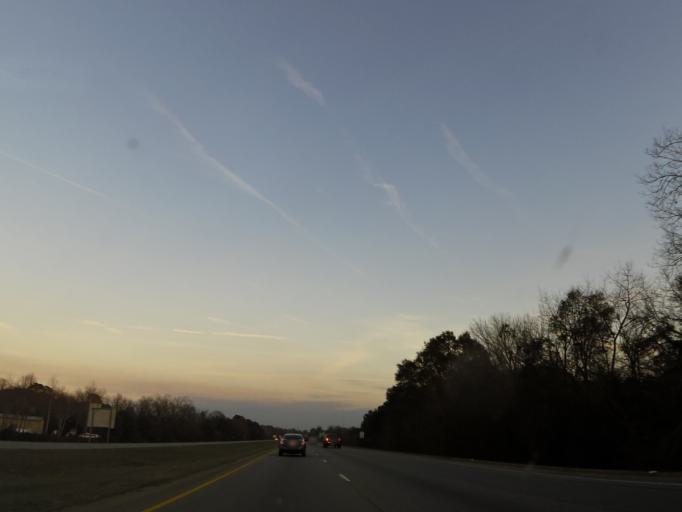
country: US
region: Georgia
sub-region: Dougherty County
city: Albany
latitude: 31.6146
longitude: -84.1713
